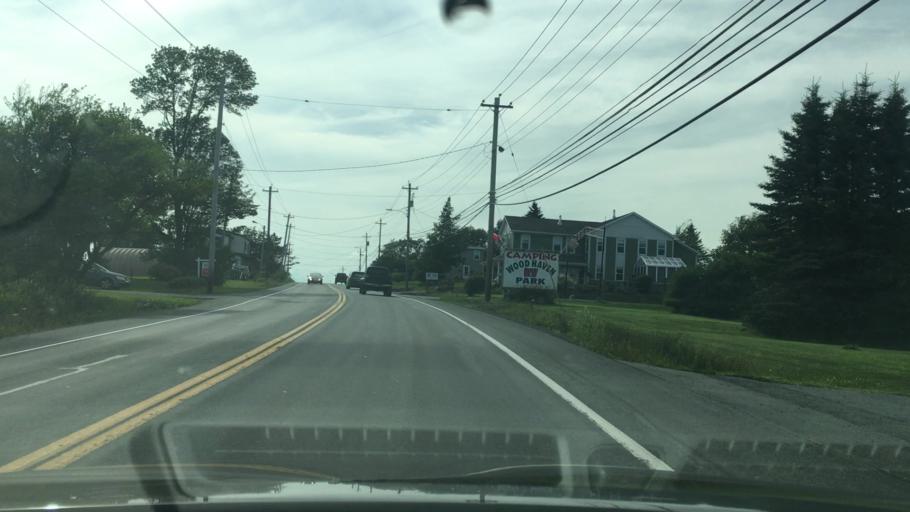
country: CA
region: Nova Scotia
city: Dartmouth
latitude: 44.7334
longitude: -63.7633
